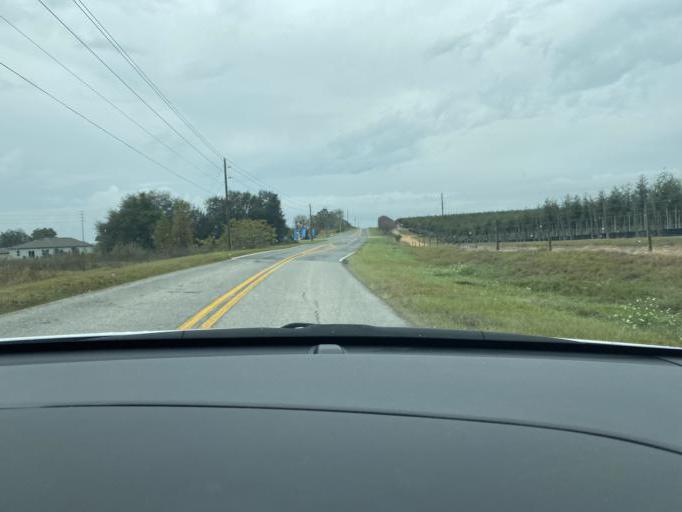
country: US
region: Florida
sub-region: Lake County
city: Groveland
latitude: 28.5874
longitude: -81.8417
